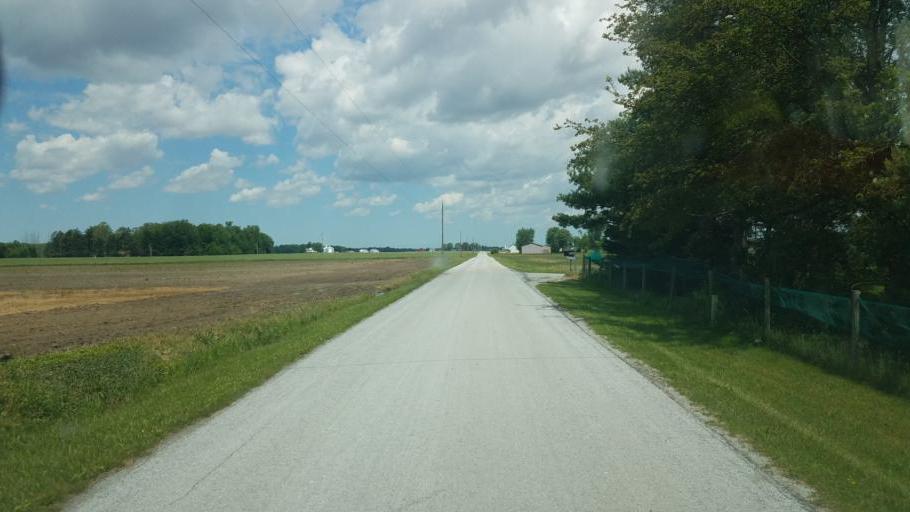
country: US
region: Ohio
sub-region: Hardin County
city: Forest
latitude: 40.6827
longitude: -83.4778
